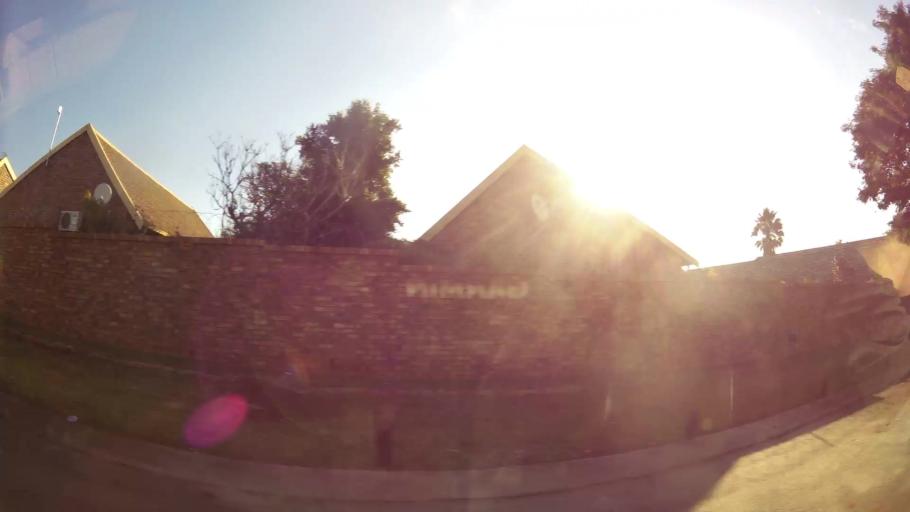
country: ZA
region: Gauteng
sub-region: City of Tshwane Metropolitan Municipality
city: Centurion
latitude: -25.8776
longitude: 28.1421
